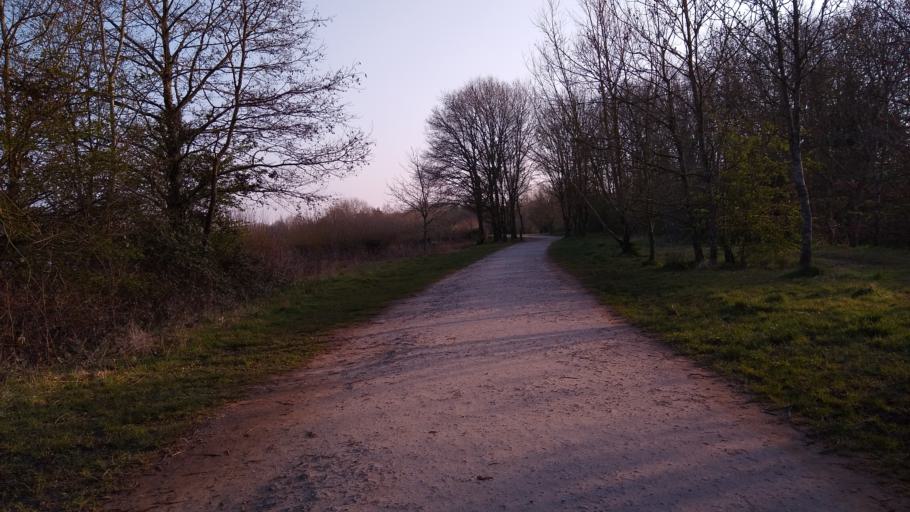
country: GB
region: England
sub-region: Wokingham
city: Woodley
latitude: 51.4436
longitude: -0.8729
